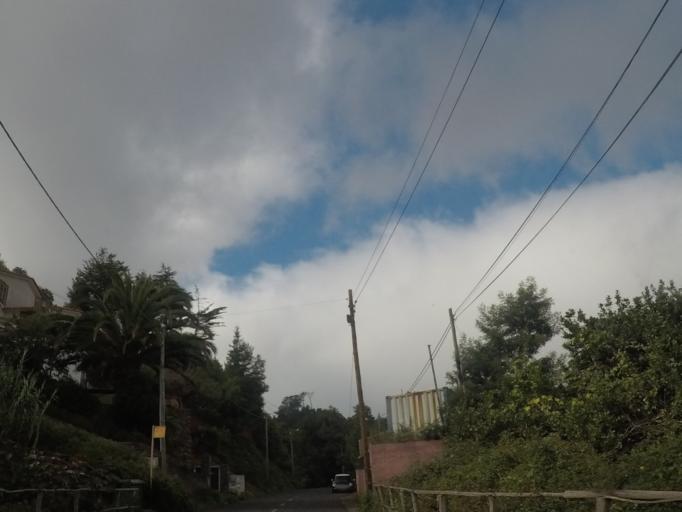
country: PT
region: Madeira
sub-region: Santa Cruz
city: Camacha
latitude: 32.6798
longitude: -16.8539
